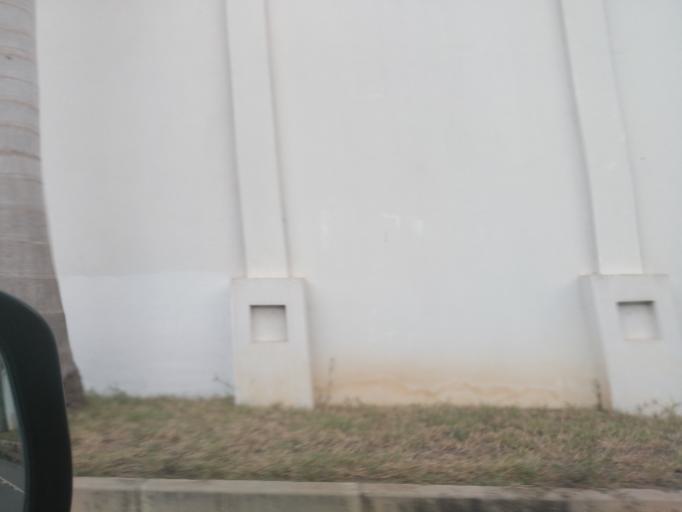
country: GH
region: Greater Accra
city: Accra
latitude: 5.6052
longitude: -0.1808
